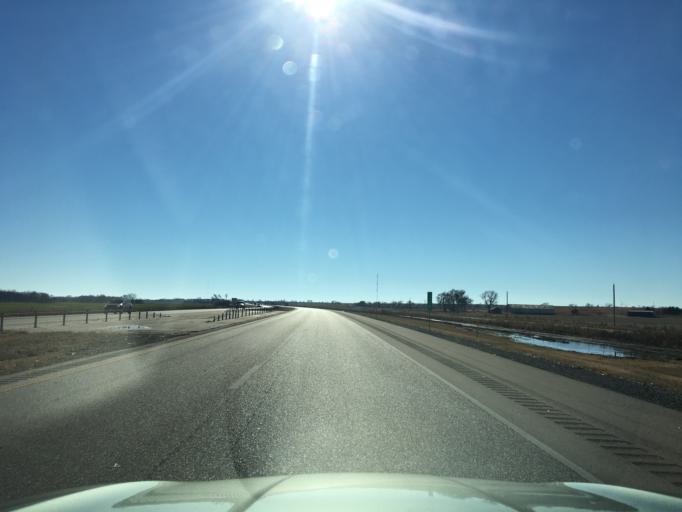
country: US
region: Oklahoma
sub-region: Kay County
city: Blackwell
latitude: 36.8989
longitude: -97.3543
